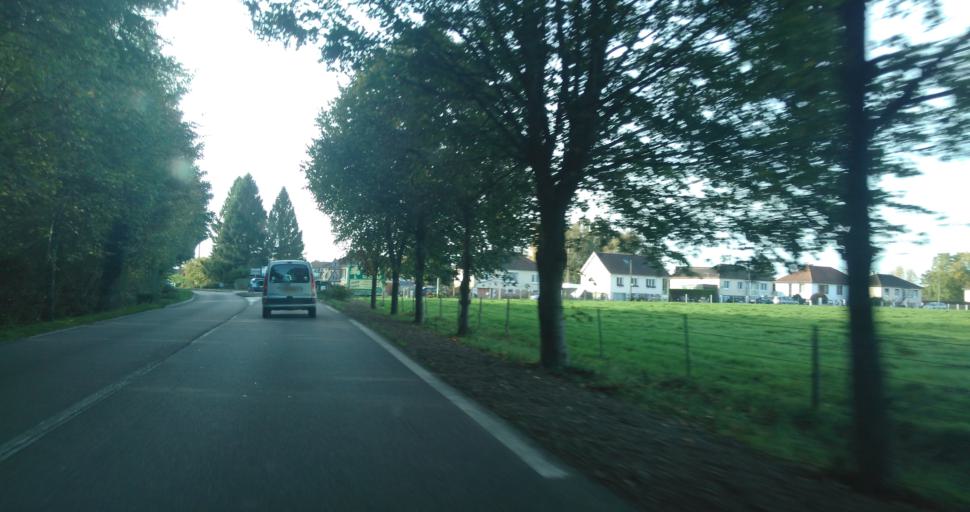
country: FR
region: Haute-Normandie
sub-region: Departement de l'Eure
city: Saint-Ouen-de-Thouberville
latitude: 49.3599
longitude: 0.8523
